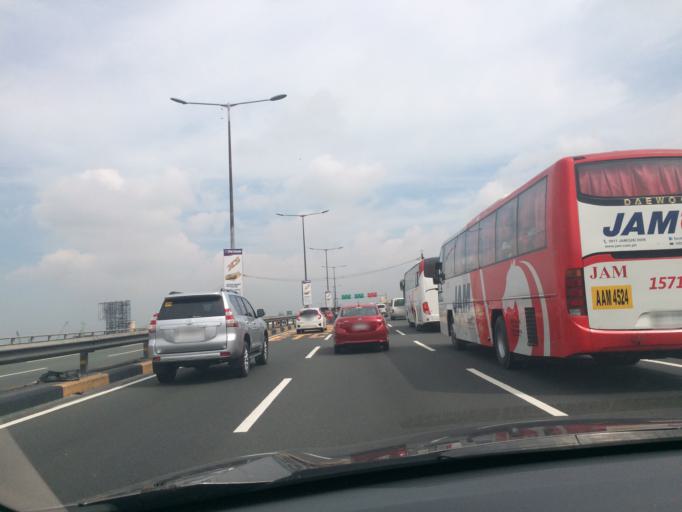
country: PH
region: Metro Manila
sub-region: Makati City
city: Makati City
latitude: 14.5071
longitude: 121.0351
